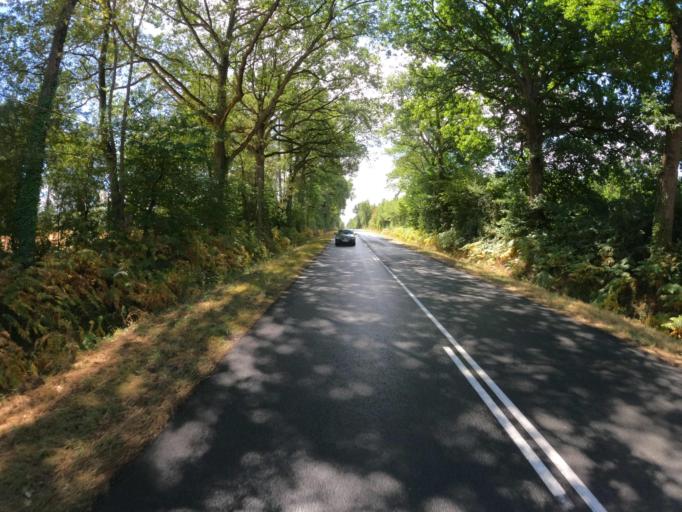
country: FR
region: Pays de la Loire
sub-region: Departement de Maine-et-Loire
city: Champigne
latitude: 47.6196
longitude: -0.5835
